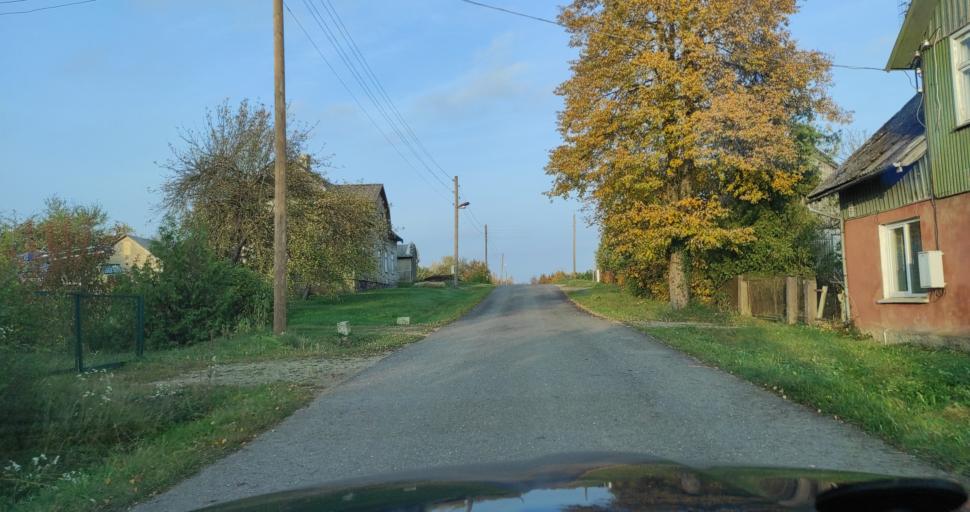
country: LV
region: Vainode
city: Vainode
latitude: 56.4178
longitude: 21.8497
